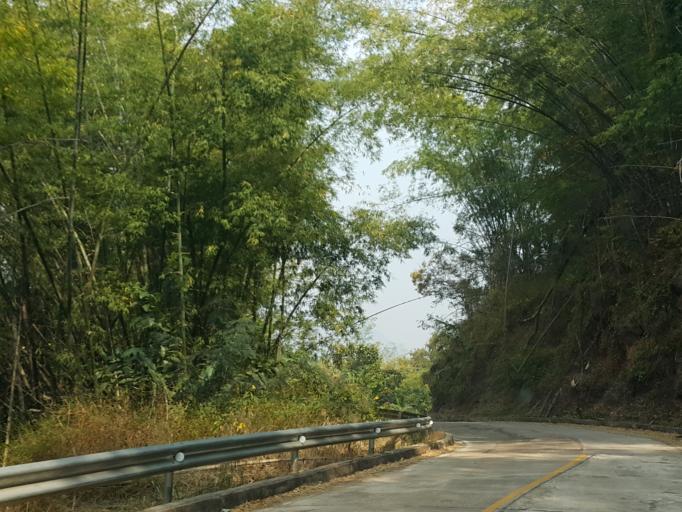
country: TH
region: Chiang Mai
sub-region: Amphoe Chiang Dao
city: Chiang Dao
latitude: 19.4116
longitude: 98.8633
